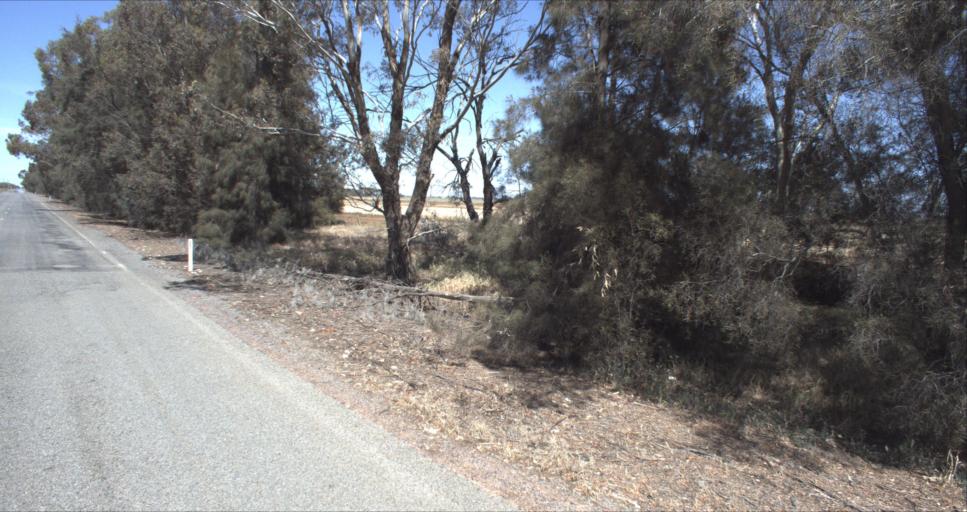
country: AU
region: New South Wales
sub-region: Leeton
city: Leeton
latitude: -34.4658
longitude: 146.2933
